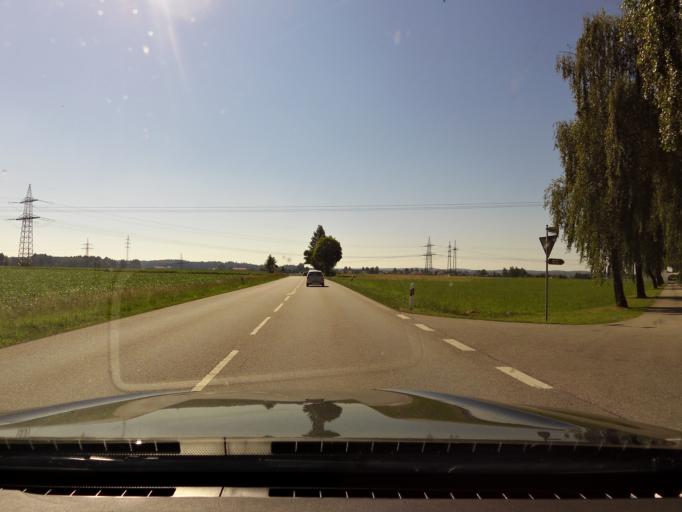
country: DE
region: Bavaria
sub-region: Upper Bavaria
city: Burgkirchen an der Alz
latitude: 48.1536
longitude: 12.7493
